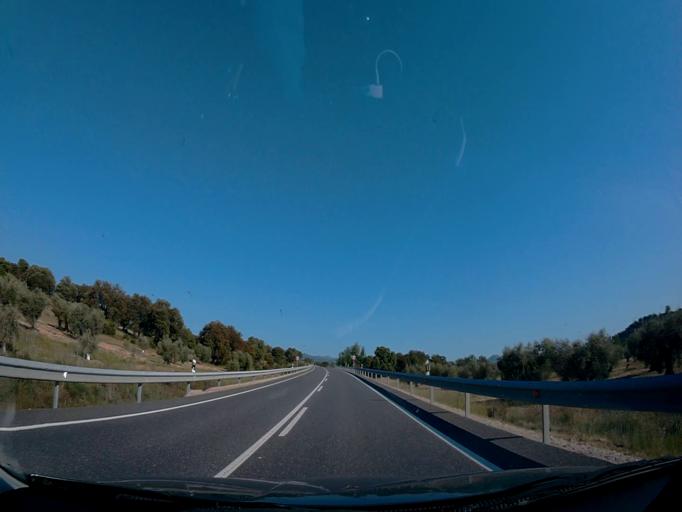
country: ES
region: Castille-La Mancha
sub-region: Province of Toledo
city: Escalona
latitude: 40.1838
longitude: -4.4010
